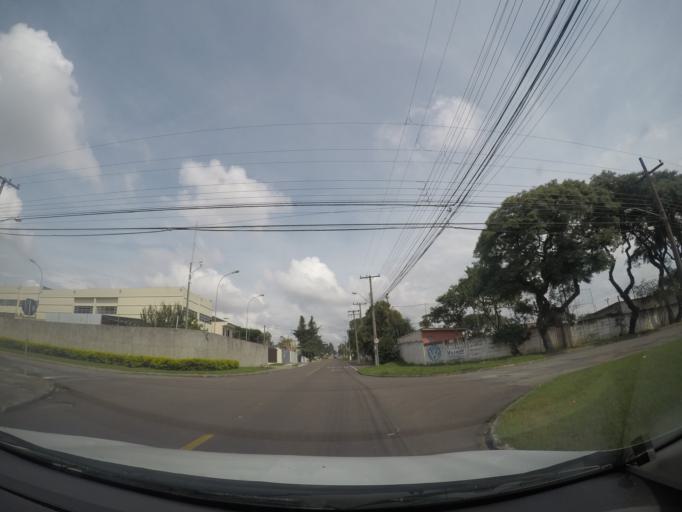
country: BR
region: Parana
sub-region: Curitiba
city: Curitiba
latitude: -25.4795
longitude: -49.2643
